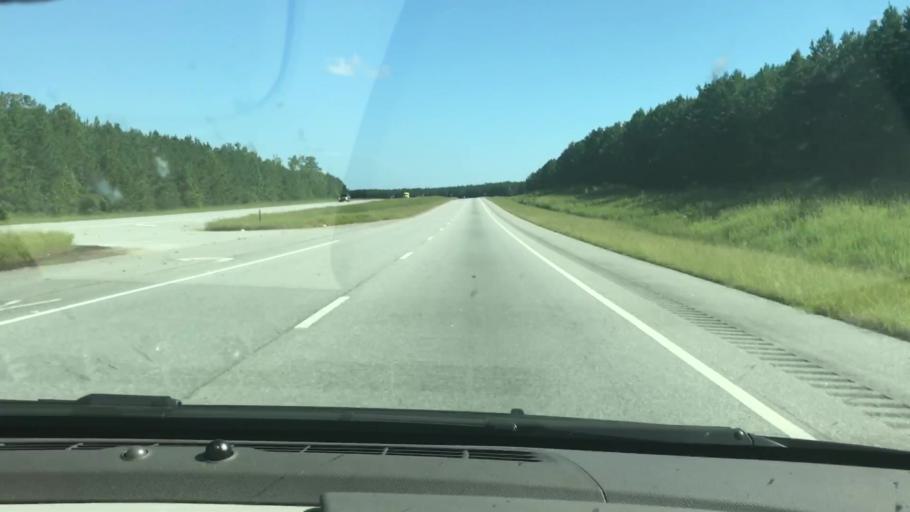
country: US
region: Alabama
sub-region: Russell County
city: Ladonia
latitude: 32.2075
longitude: -85.1716
